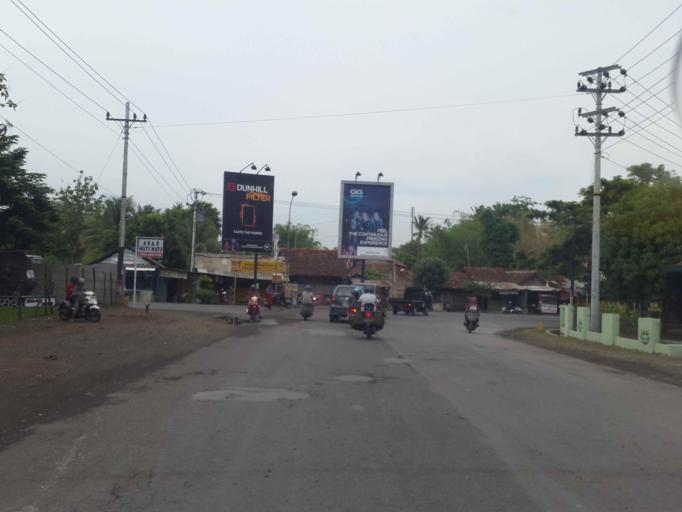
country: ID
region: Central Java
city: Adiwerna
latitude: -6.9435
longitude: 109.1254
